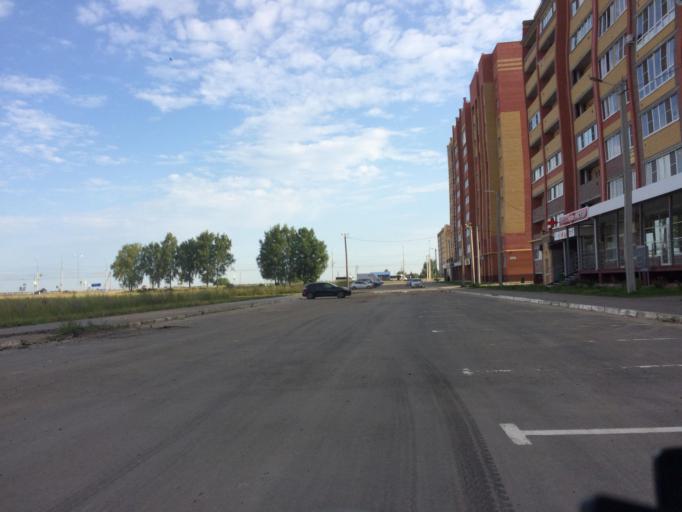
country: RU
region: Mariy-El
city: Medvedevo
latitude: 56.6379
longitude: 47.8193
